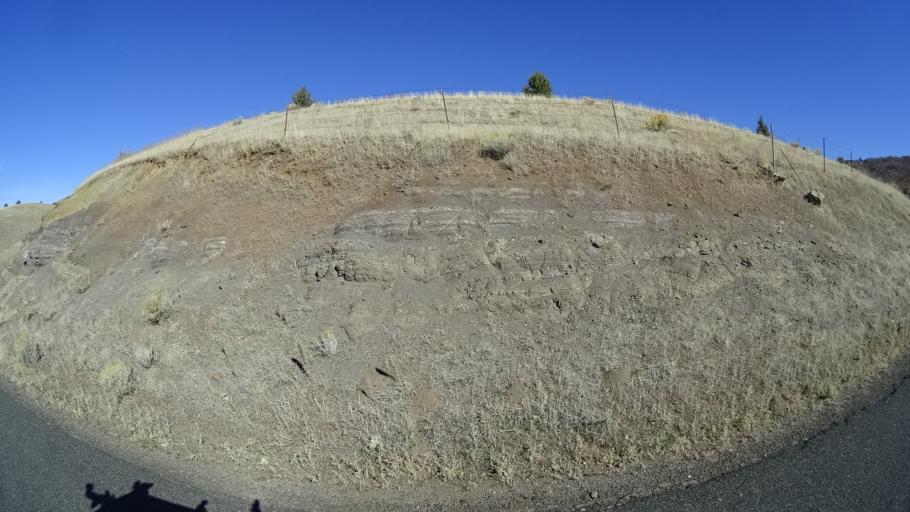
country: US
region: California
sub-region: Siskiyou County
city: Montague
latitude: 41.8237
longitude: -122.3424
